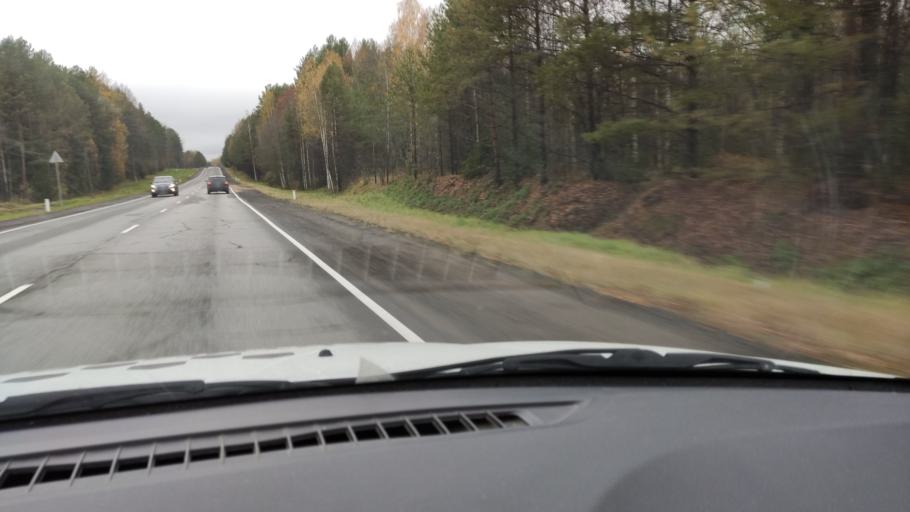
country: RU
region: Kirov
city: Belaya Kholunitsa
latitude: 58.8954
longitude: 50.9043
